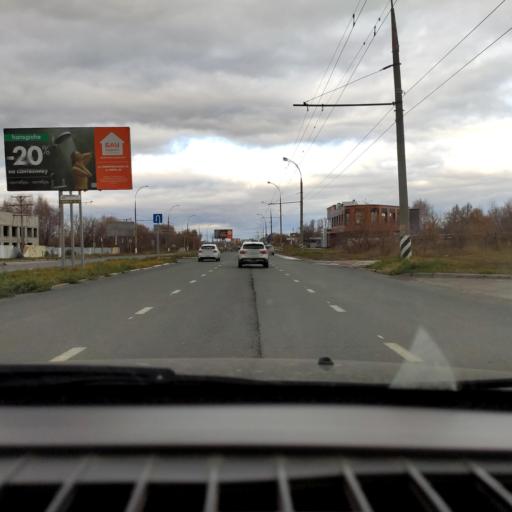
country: RU
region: Samara
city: Tol'yatti
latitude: 53.5451
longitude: 49.3015
